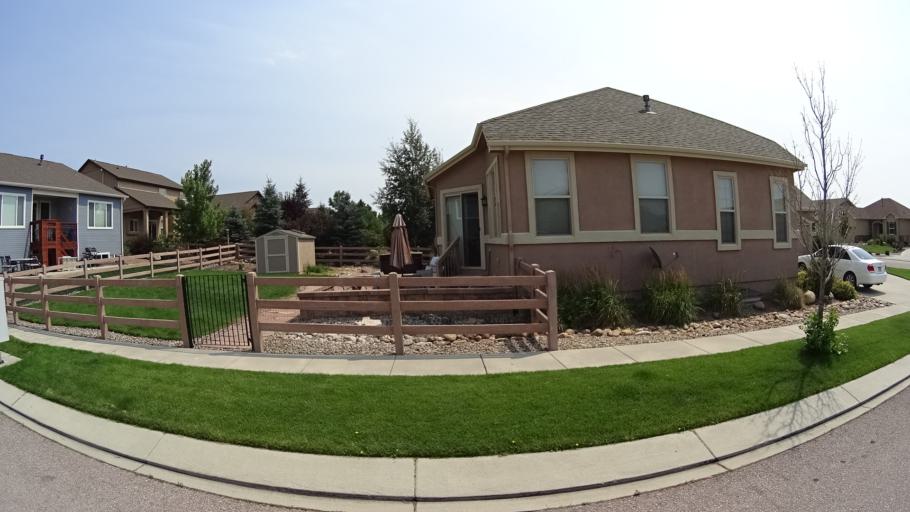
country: US
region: Colorado
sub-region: El Paso County
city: Black Forest
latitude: 38.9653
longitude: -104.7188
